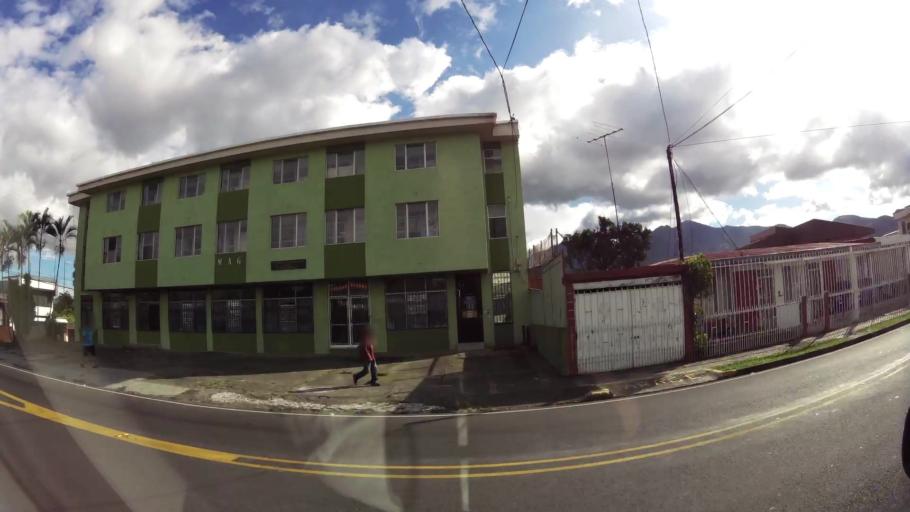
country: CR
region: San Jose
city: San Rafael
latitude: 9.9333
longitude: -84.1189
